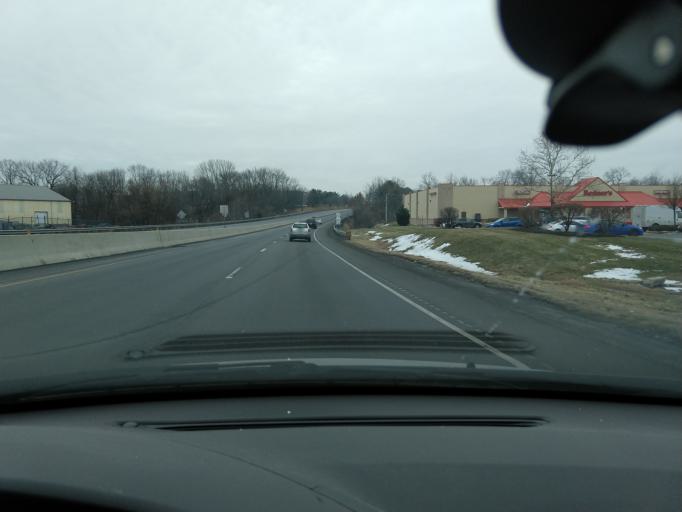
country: US
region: Pennsylvania
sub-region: Berks County
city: Boyertown
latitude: 40.3337
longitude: -75.6210
